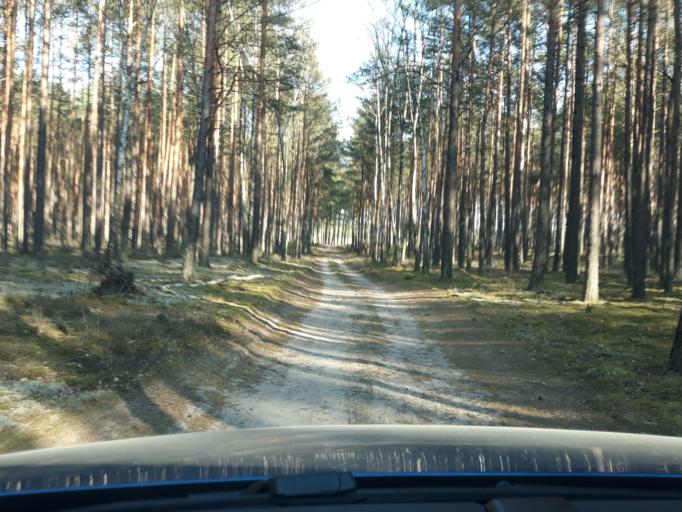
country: PL
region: Pomeranian Voivodeship
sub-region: Powiat bytowski
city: Lipnica
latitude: 53.9179
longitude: 17.4667
